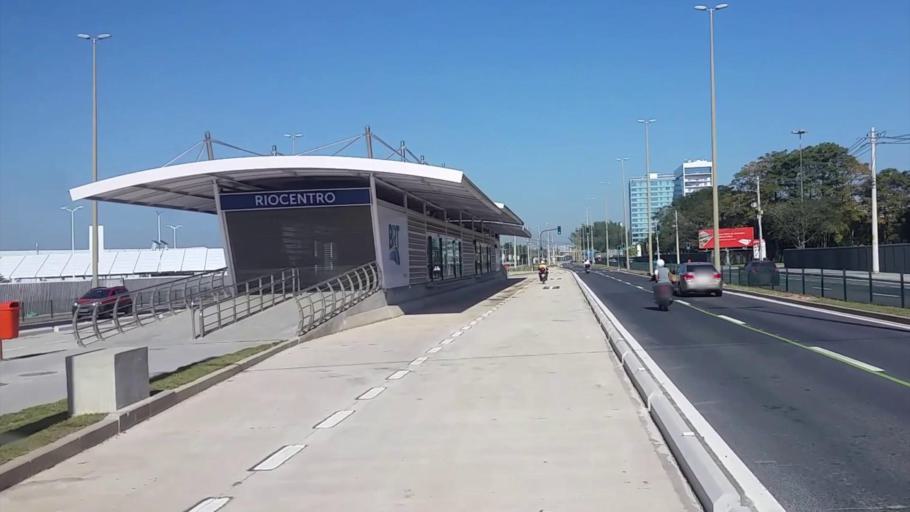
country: BR
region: Rio de Janeiro
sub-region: Nilopolis
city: Nilopolis
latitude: -22.9694
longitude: -43.3995
